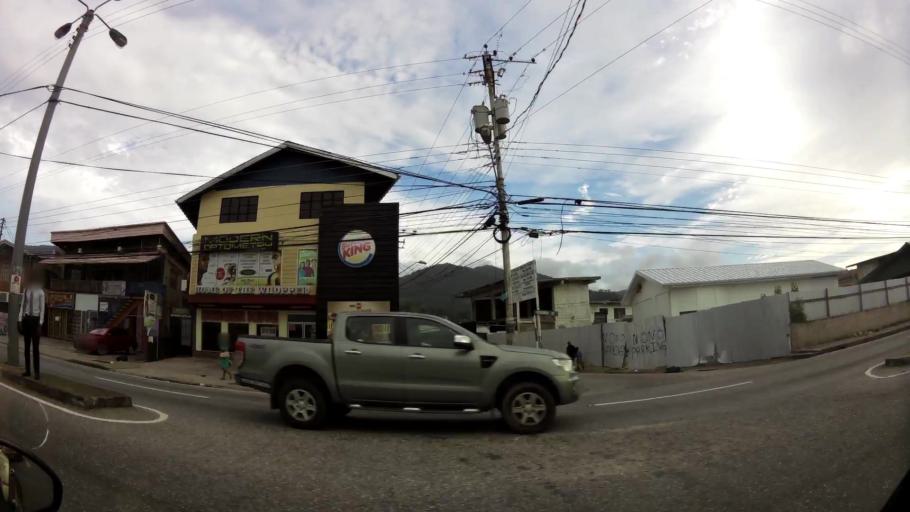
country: TT
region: Tunapuna/Piarco
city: Tunapuna
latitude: 10.6506
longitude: -61.4106
